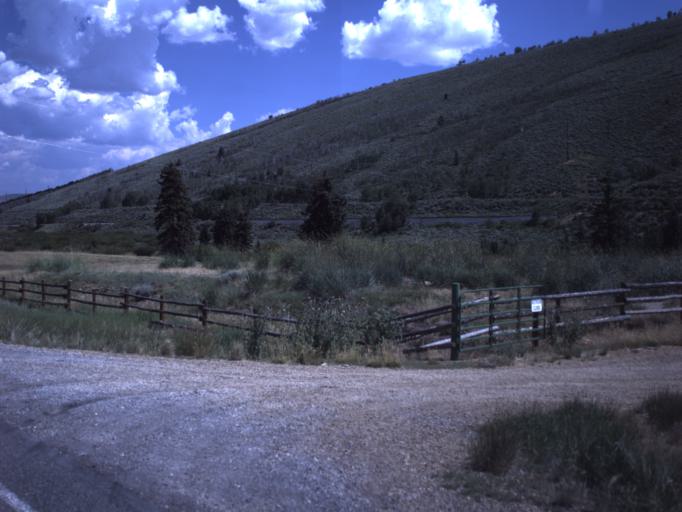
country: US
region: Utah
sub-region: Sanpete County
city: Fairview
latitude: 39.7082
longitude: -111.1632
